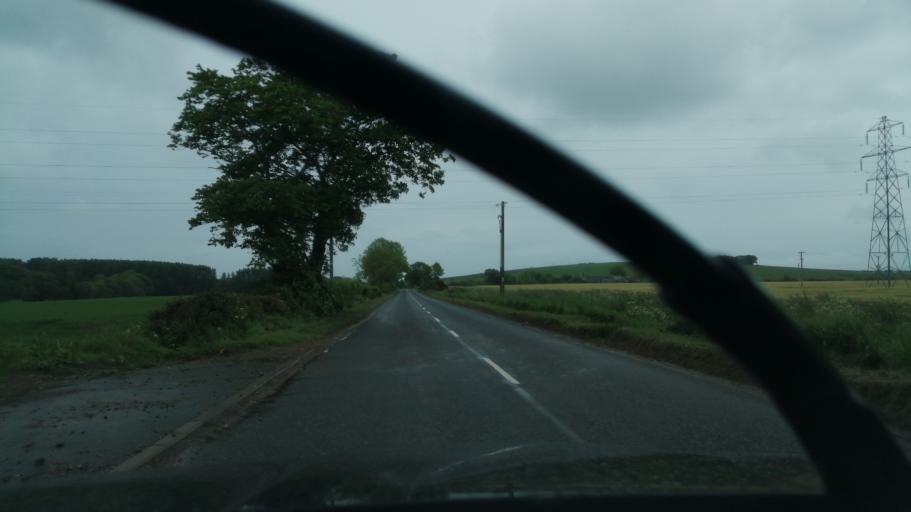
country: GB
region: Scotland
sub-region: Aberdeenshire
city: Portsoy
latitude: 57.6687
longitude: -2.6908
